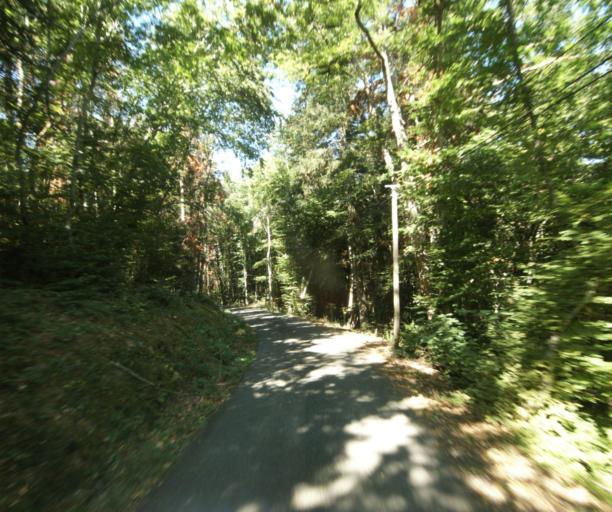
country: FR
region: Rhone-Alpes
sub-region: Departement du Rhone
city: Montrottier
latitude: 45.8107
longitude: 4.5001
